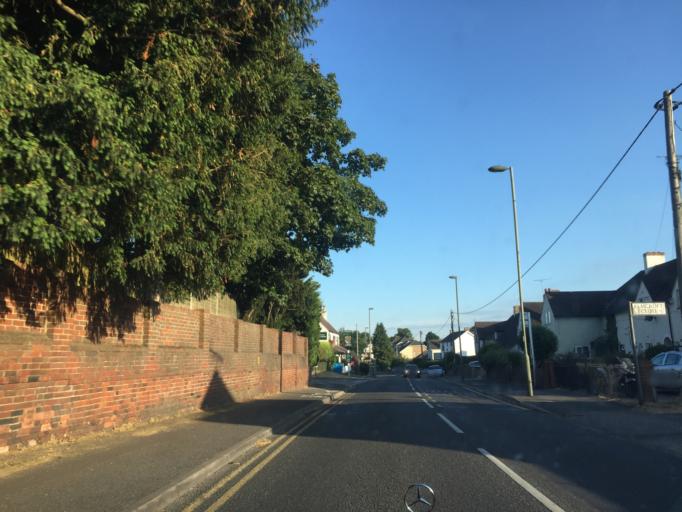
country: GB
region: England
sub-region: Surrey
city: Frimley
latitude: 51.3060
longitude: -0.7297
